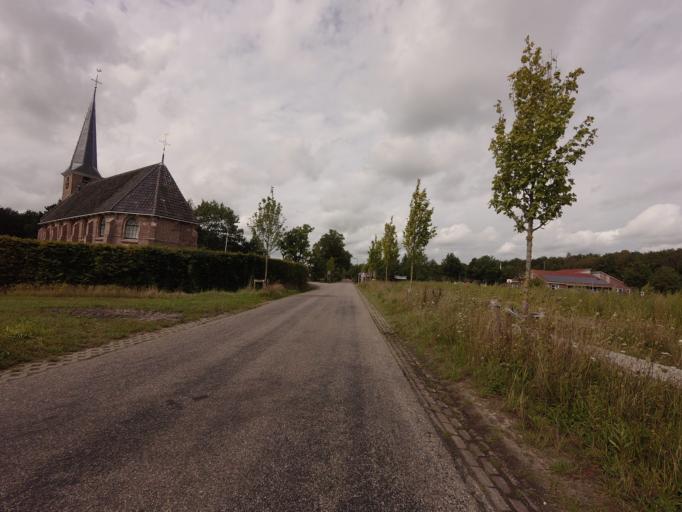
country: NL
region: Friesland
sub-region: Gemeente Heerenveen
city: Nieuwehorne
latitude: 52.9106
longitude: 6.0803
